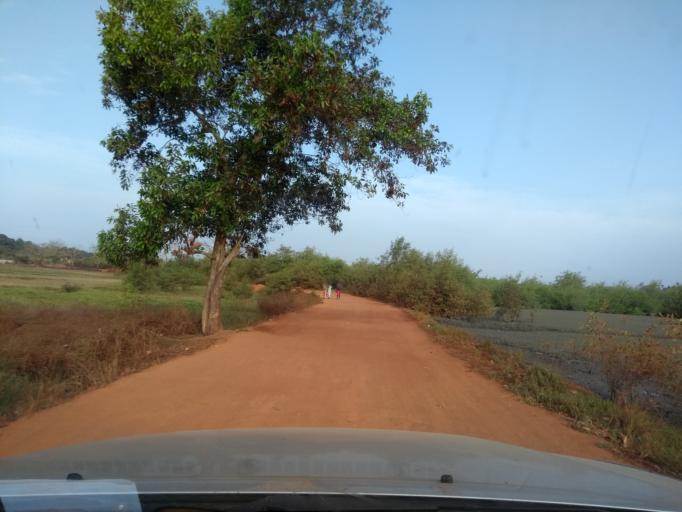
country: GN
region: Kindia
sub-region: Prefecture de Dubreka
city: Dubreka
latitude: 9.7893
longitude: -13.5291
